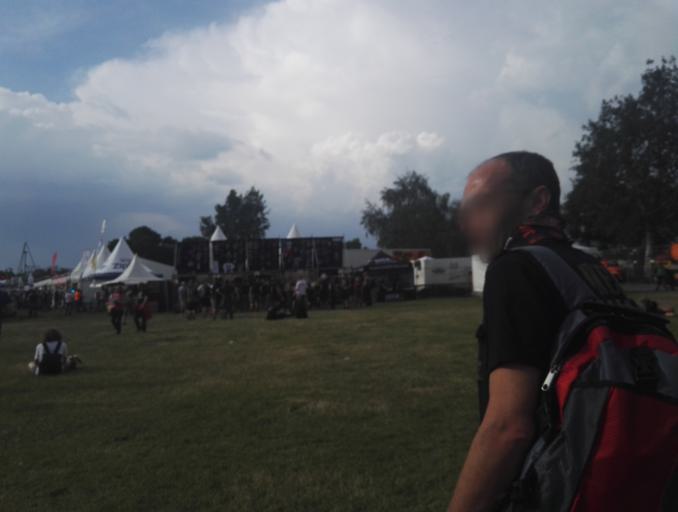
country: AT
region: Vienna
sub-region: Wien Stadt
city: Vienna
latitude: 48.2454
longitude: 16.3907
